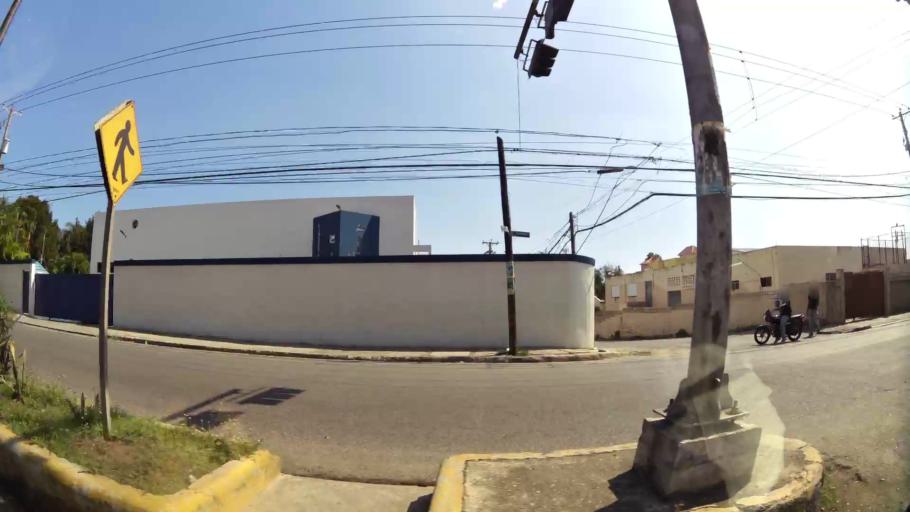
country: DO
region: Nacional
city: Santo Domingo
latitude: 18.4851
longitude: -69.9878
